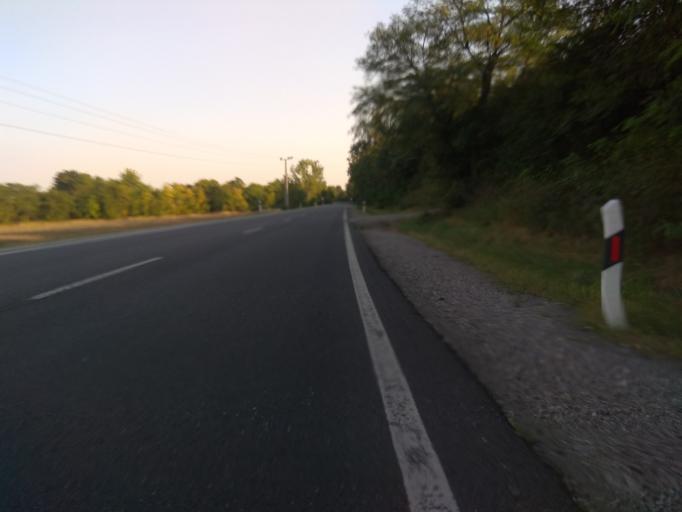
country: HU
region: Borsod-Abauj-Zemplen
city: Nyekladhaza
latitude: 47.9624
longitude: 20.8340
